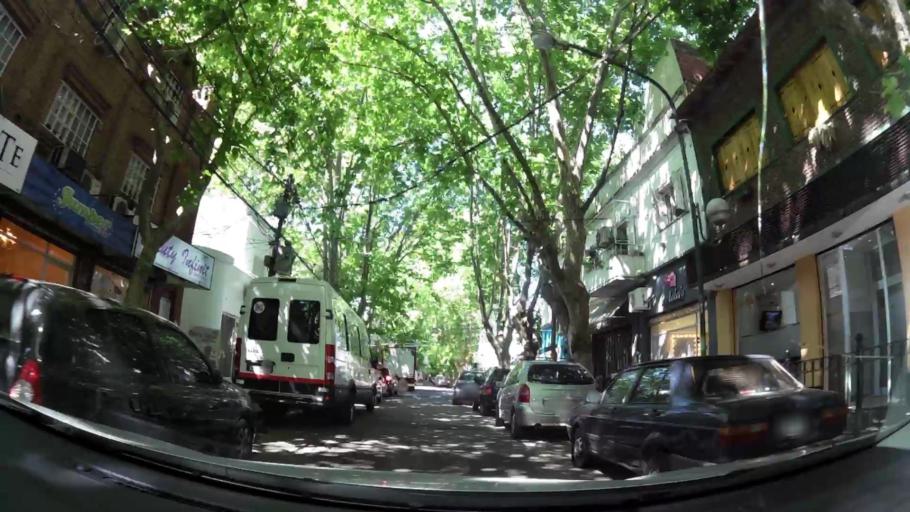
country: AR
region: Buenos Aires
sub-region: Partido de Vicente Lopez
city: Olivos
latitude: -34.5231
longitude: -58.4741
